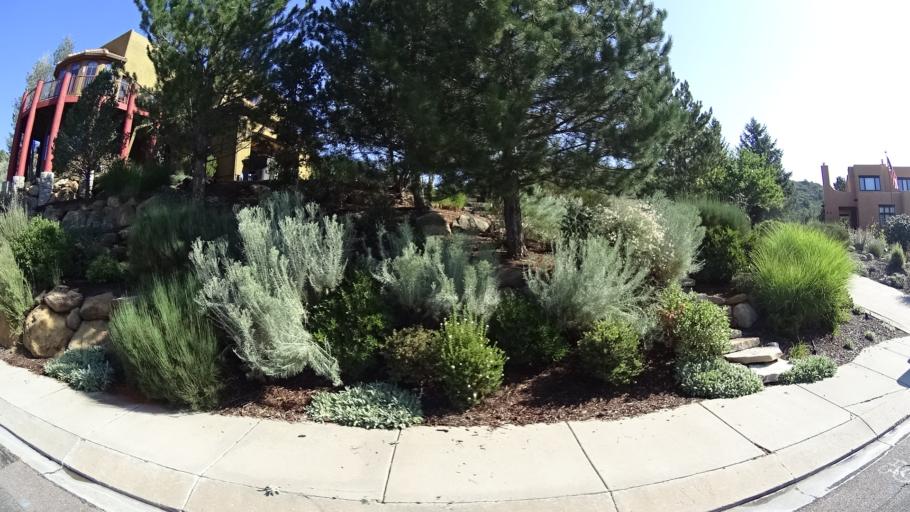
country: US
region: Colorado
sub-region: El Paso County
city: Colorado Springs
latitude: 38.8791
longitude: -104.7871
